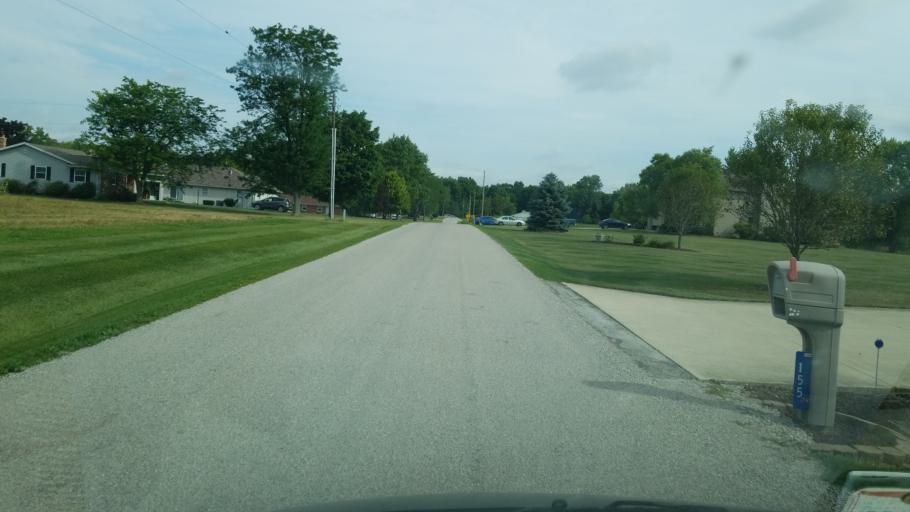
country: US
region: Ohio
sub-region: Seneca County
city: Tiffin
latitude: 41.1267
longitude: -83.0933
